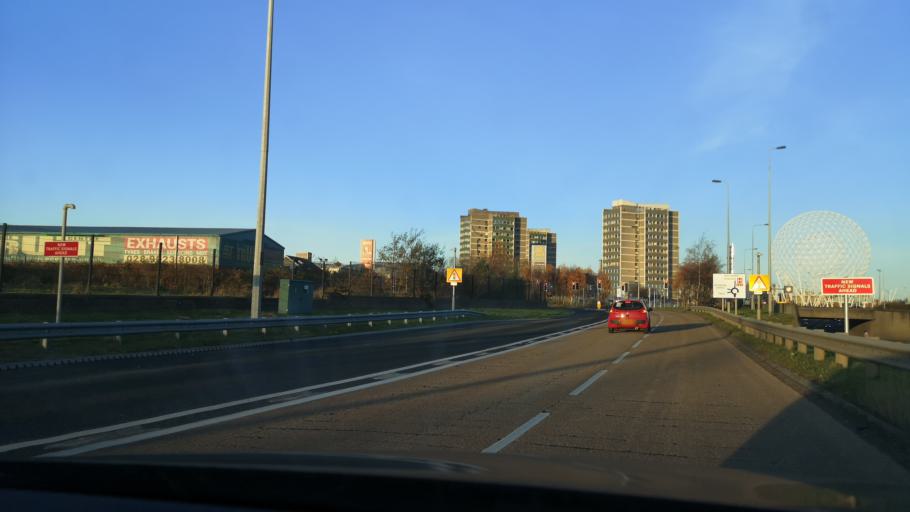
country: GB
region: Northern Ireland
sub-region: City of Belfast
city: Belfast
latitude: 54.5867
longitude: -5.9611
